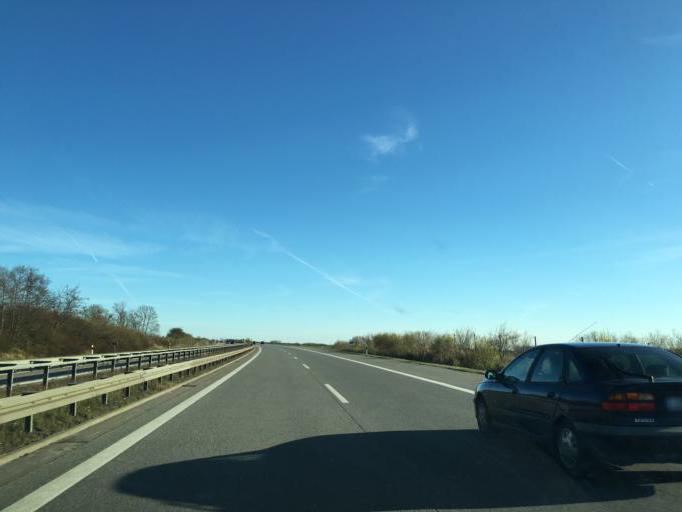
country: DE
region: Mecklenburg-Vorpommern
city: Kavelstorf
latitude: 53.9548
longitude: 12.1981
